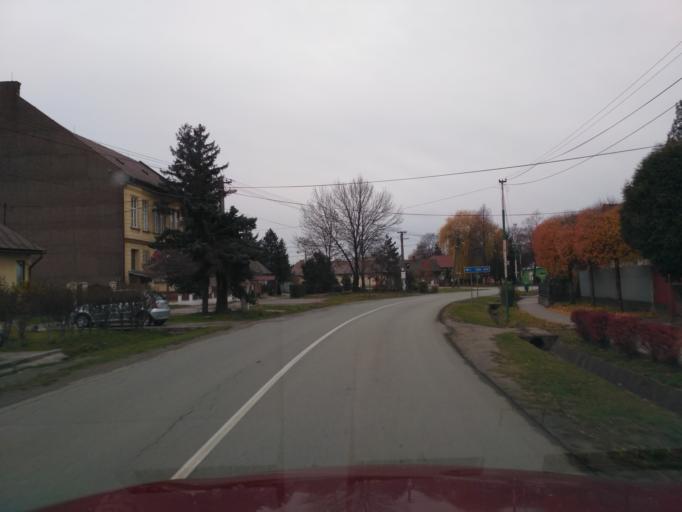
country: SK
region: Kosicky
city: Kosice
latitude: 48.5939
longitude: 21.1686
